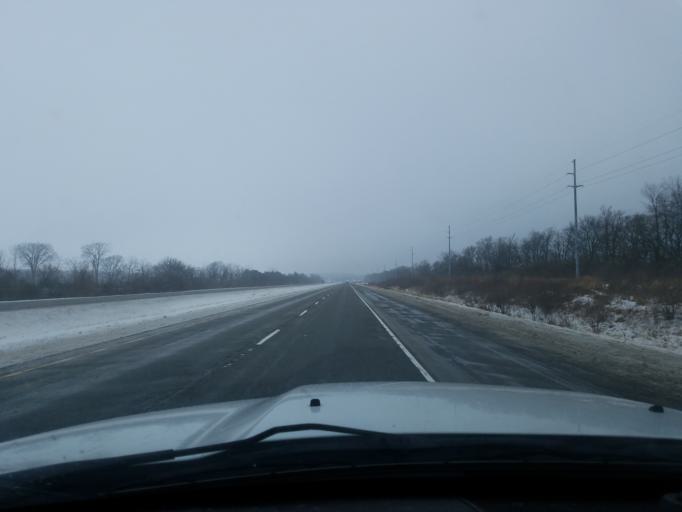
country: US
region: Indiana
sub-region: Fulton County
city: Rochester
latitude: 41.0205
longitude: -86.1752
